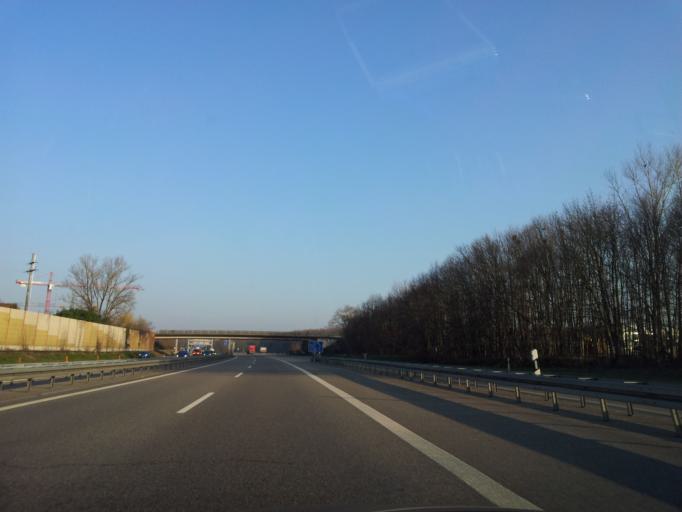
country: DE
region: Baden-Wuerttemberg
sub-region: Freiburg Region
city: Weil am Rhein
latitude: 47.6033
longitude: 7.6012
